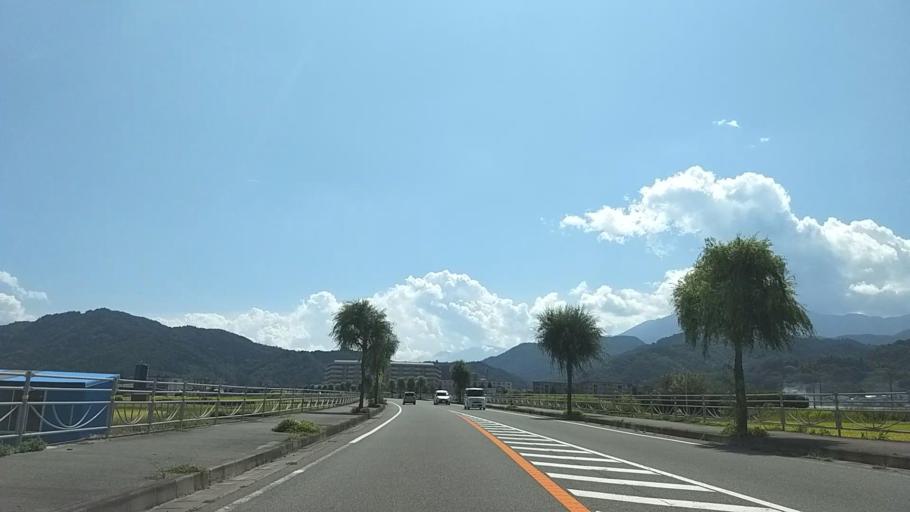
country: JP
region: Yamanashi
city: Ryuo
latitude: 35.5553
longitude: 138.4689
